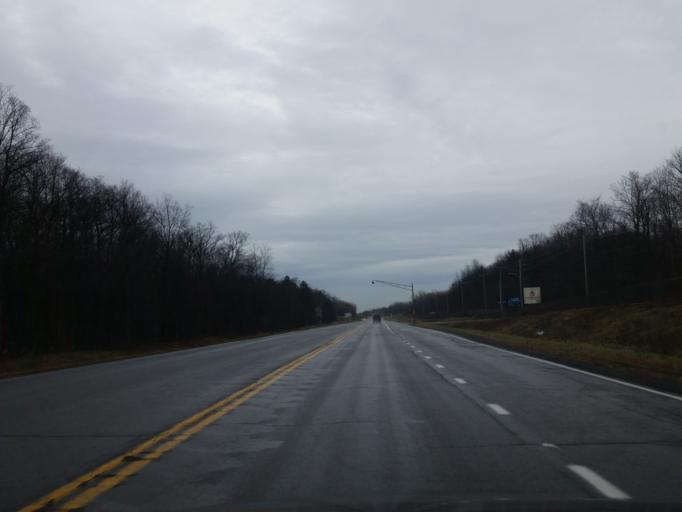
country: CA
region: Quebec
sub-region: Laurentides
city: Mirabel
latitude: 45.6844
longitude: -74.0810
